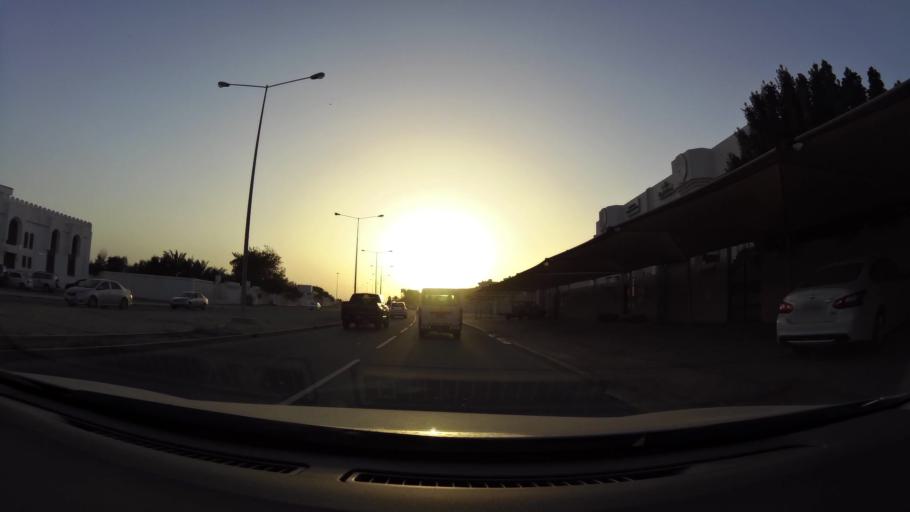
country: QA
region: Baladiyat ar Rayyan
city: Ar Rayyan
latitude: 25.3133
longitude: 51.4637
